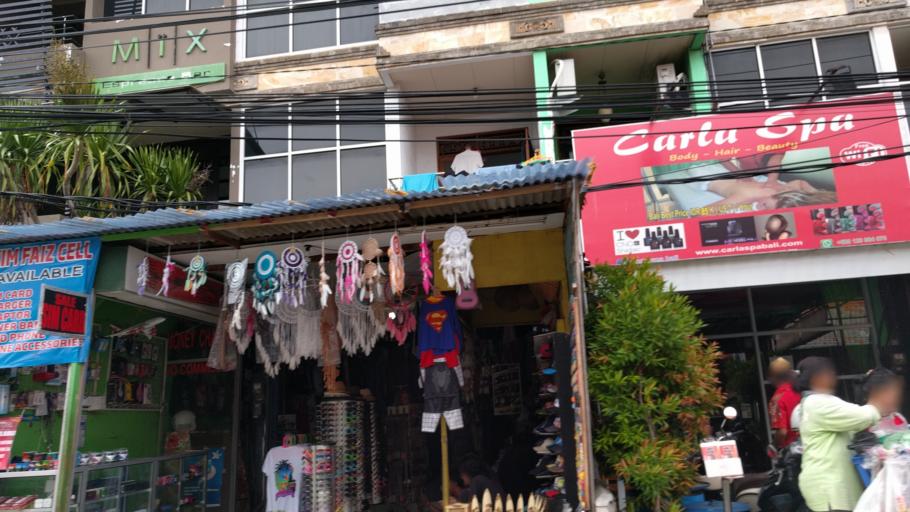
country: ID
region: Bali
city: Kuta
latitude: -8.6918
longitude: 115.1633
